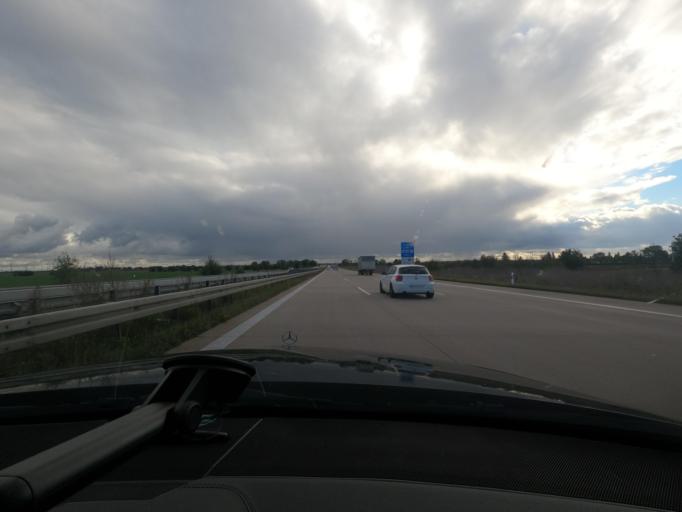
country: DE
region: Saxony-Anhalt
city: Thalheim
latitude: 51.6213
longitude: 12.1903
